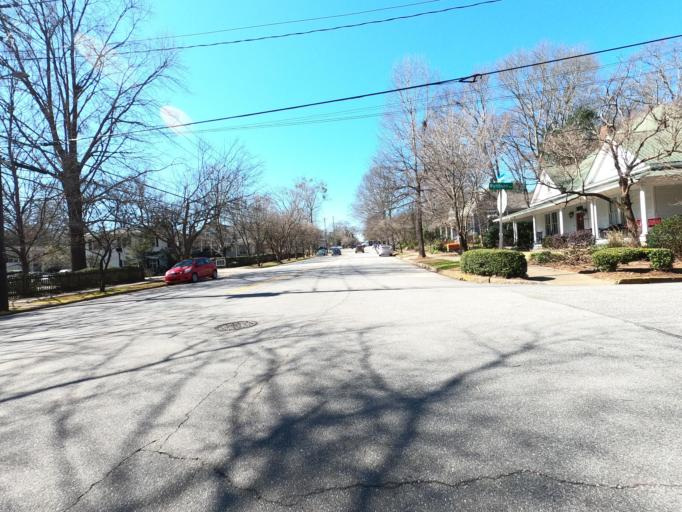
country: US
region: Georgia
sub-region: Clarke County
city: Athens
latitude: 33.9659
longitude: -83.3914
